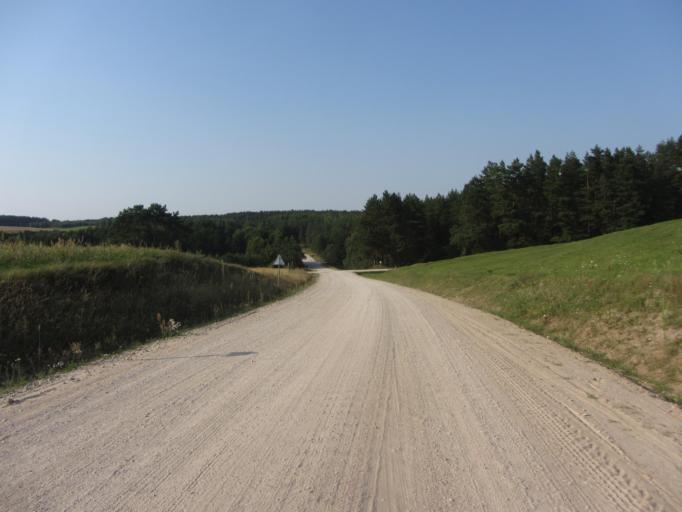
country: LT
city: Lazdijai
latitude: 54.1027
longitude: 23.5385
